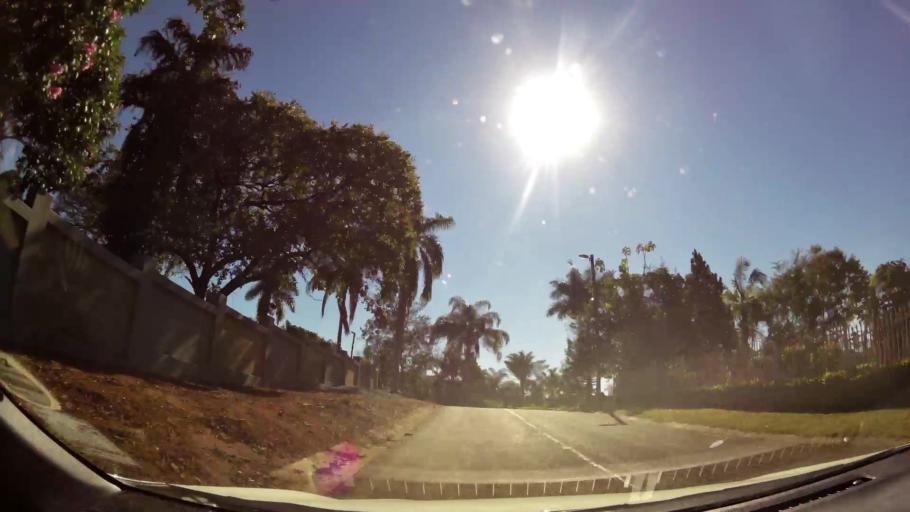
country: ZA
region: Limpopo
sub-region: Mopani District Municipality
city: Tzaneen
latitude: -23.8265
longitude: 30.1453
